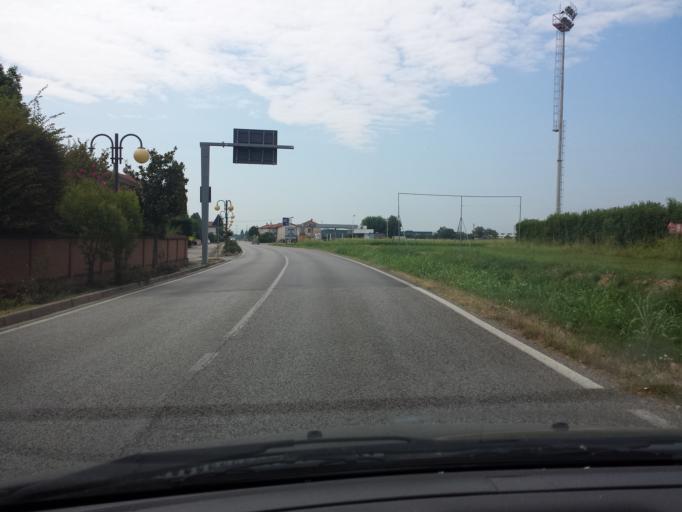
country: IT
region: Veneto
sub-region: Provincia di Vicenza
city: Breganze
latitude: 45.7001
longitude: 11.5640
